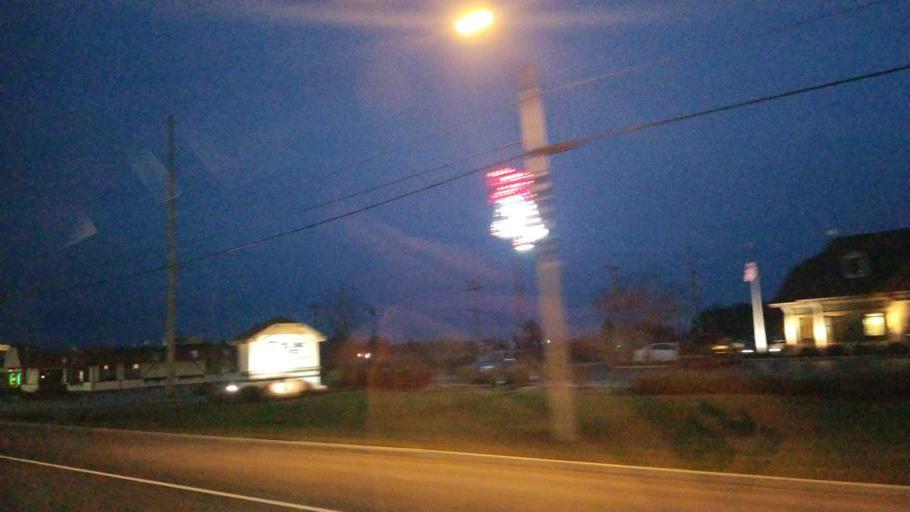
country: US
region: Indiana
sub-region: Adams County
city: Berne
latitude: 40.6682
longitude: -84.9556
